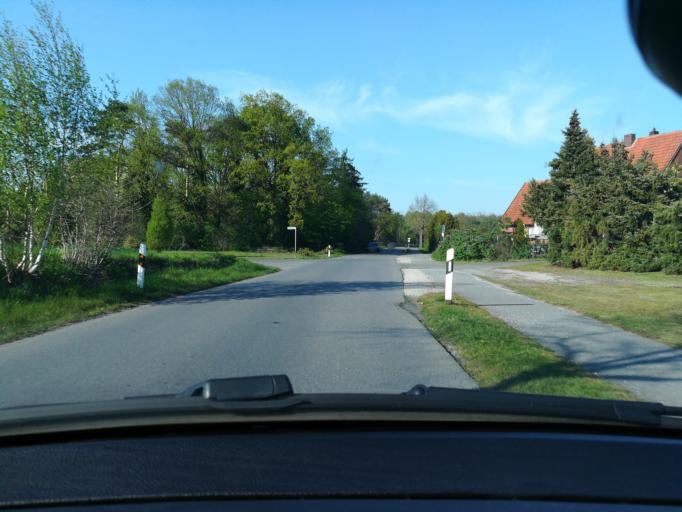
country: DE
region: North Rhine-Westphalia
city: Versmold
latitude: 52.0193
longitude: 8.1324
